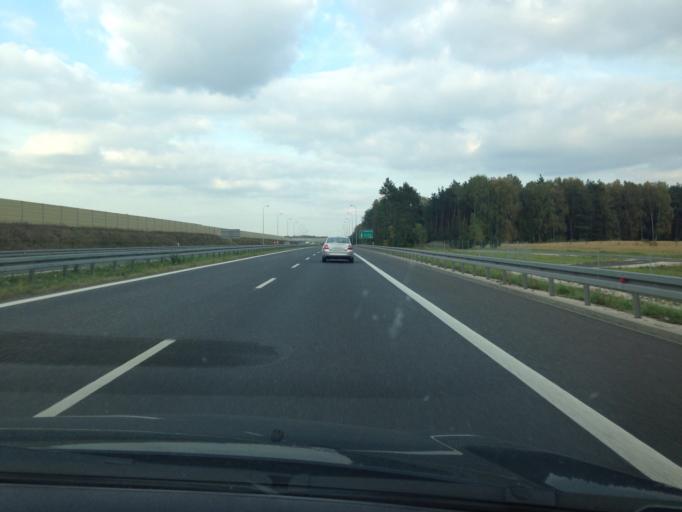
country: PL
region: Greater Poland Voivodeship
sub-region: Powiat poznanski
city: Pobiedziska
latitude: 52.4516
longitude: 17.3757
